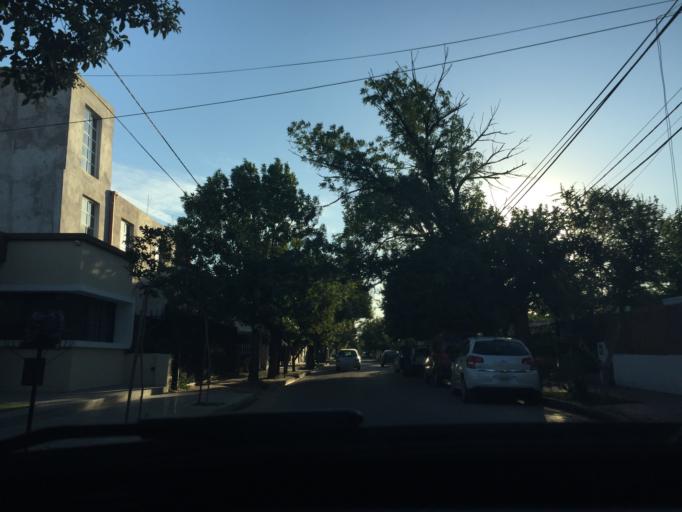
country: AR
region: Cordoba
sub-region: Departamento de Capital
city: Cordoba
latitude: -31.3648
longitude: -64.2324
